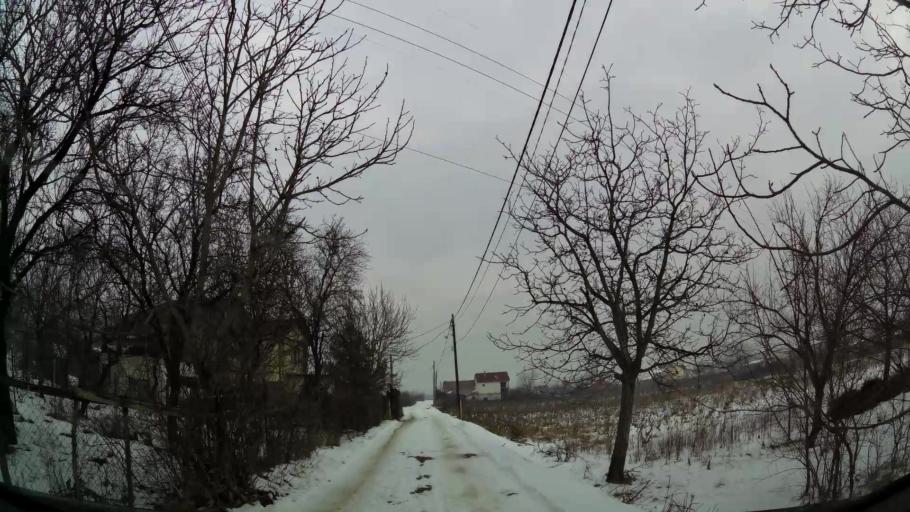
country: MK
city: Kondovo
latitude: 42.0385
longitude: 21.3395
